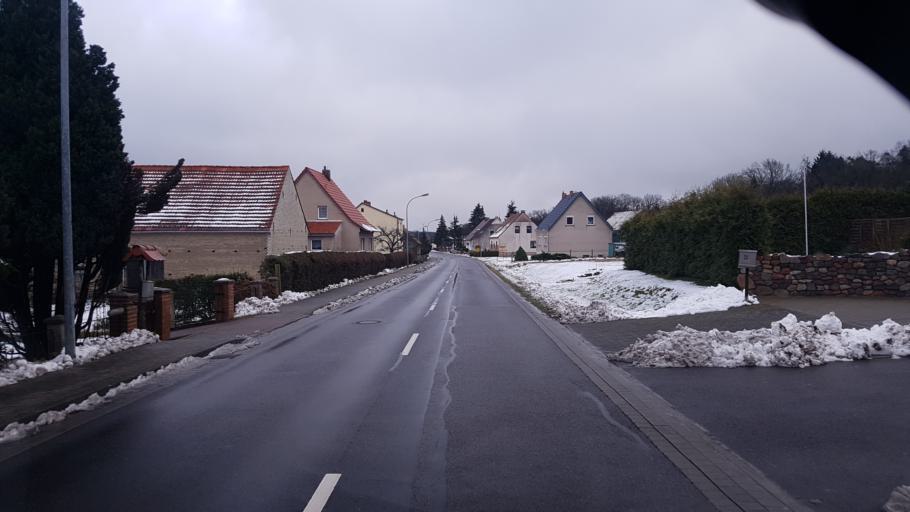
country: DE
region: Brandenburg
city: Schenkendobern
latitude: 51.9718
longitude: 14.5667
